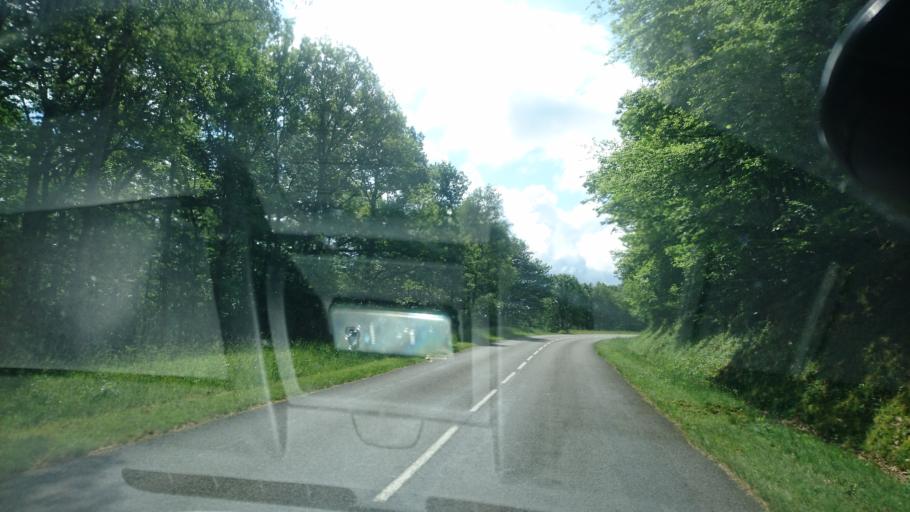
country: FR
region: Limousin
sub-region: Departement de la Haute-Vienne
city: Peyrat-le-Chateau
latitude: 45.7942
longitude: 1.8497
